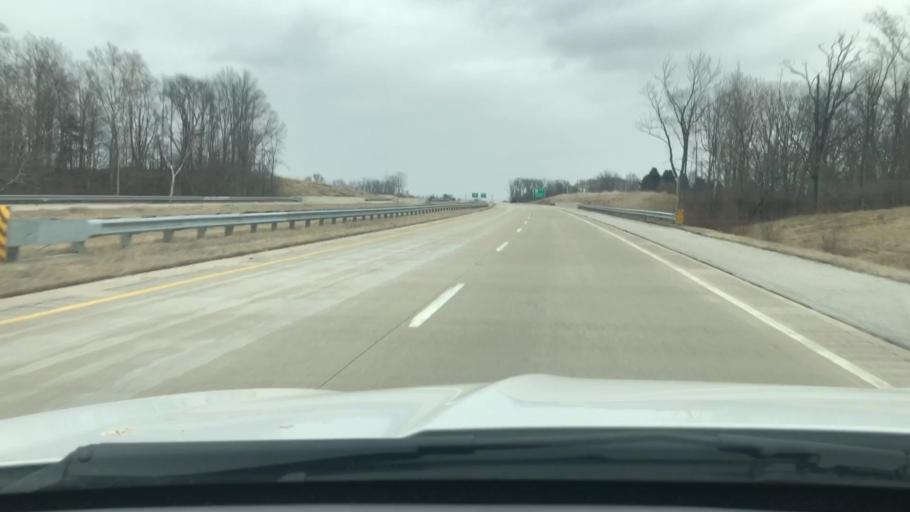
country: US
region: Indiana
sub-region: Cass County
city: Dunkirk
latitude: 40.7272
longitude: -86.3992
